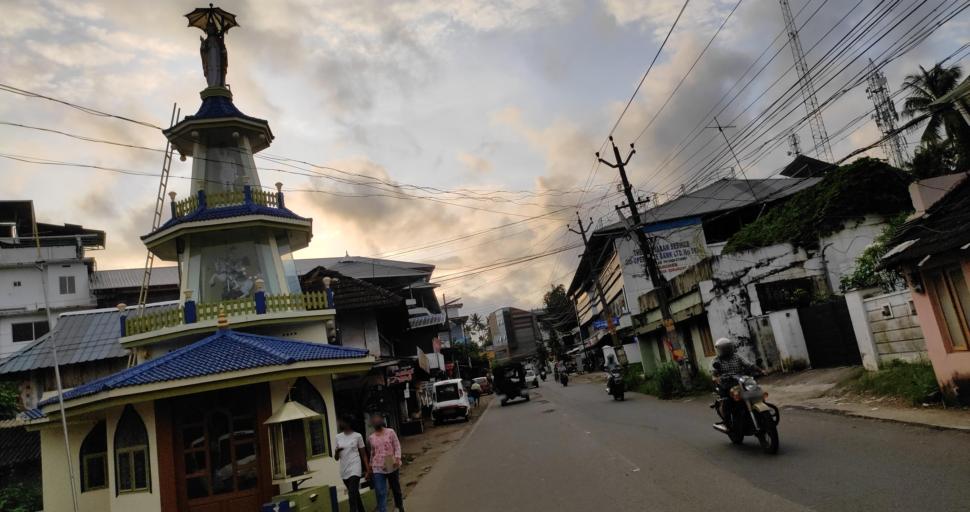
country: IN
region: Kerala
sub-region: Thrissur District
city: Kizhake Chalakudi
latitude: 10.3196
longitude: 76.3718
